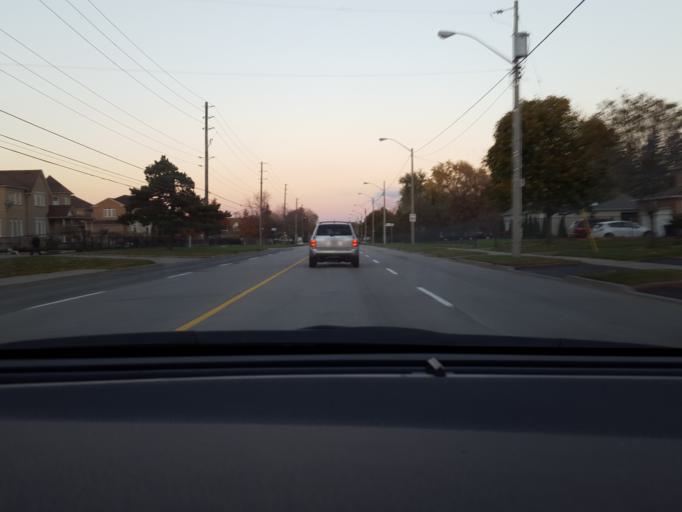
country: CA
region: Ontario
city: Scarborough
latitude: 43.7888
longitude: -79.1790
